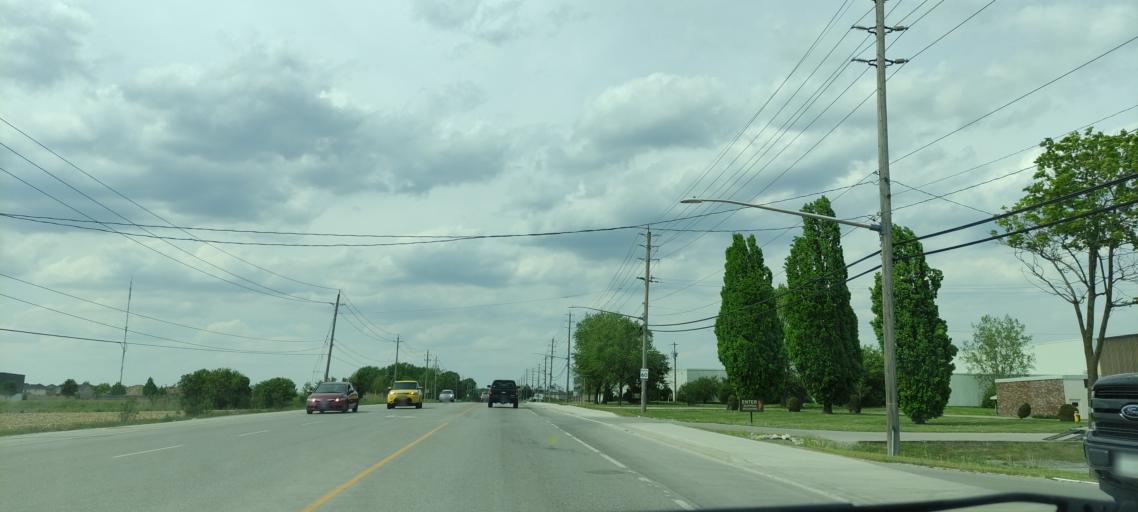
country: CA
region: Ontario
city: London
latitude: 42.9327
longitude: -81.2500
